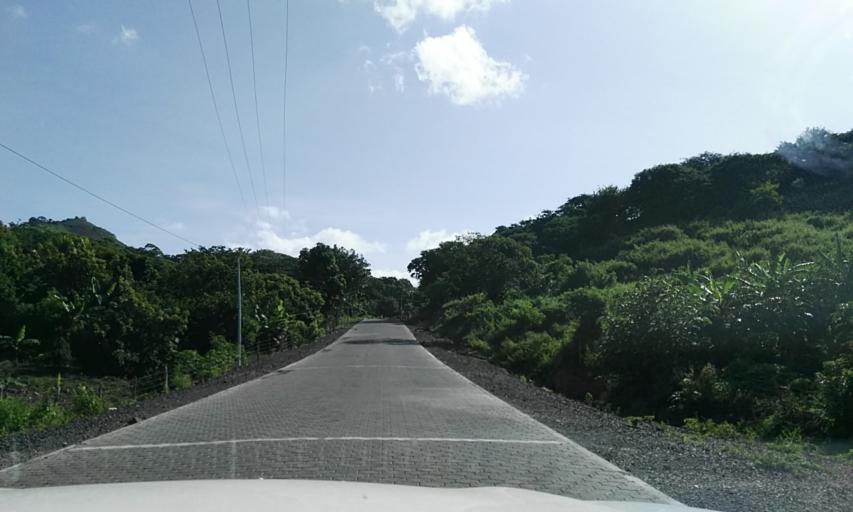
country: NI
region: Matagalpa
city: Terrabona
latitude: 12.7533
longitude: -85.9903
